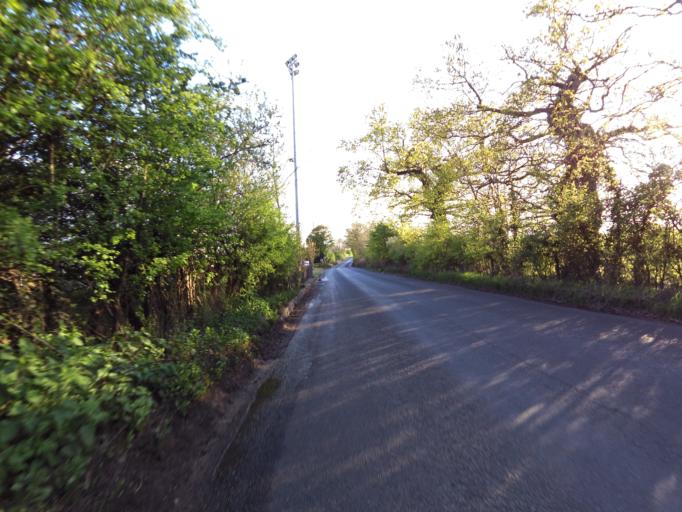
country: GB
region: England
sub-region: Suffolk
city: Ipswich
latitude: 52.0753
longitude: 1.1783
